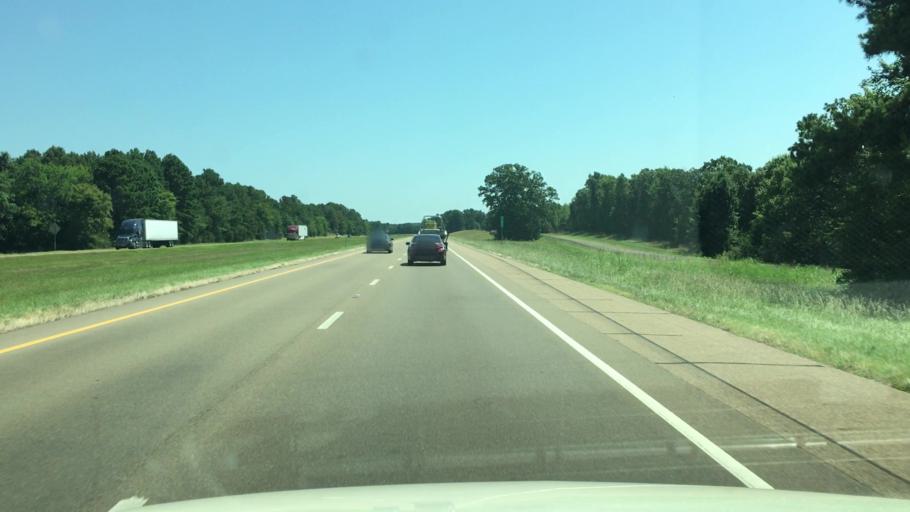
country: US
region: Texas
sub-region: Bowie County
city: De Kalb
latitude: 33.3864
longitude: -94.5990
